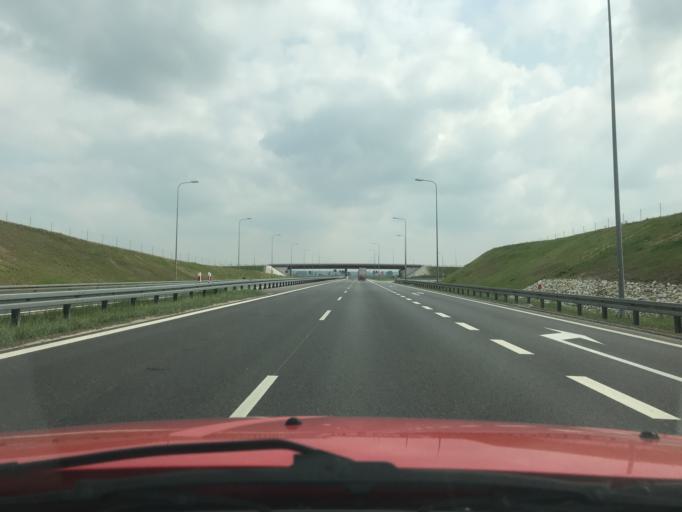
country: PL
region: Greater Poland Voivodeship
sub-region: Powiat sredzki
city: Nowe Miasto nad Warta
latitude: 52.0383
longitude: 17.4645
